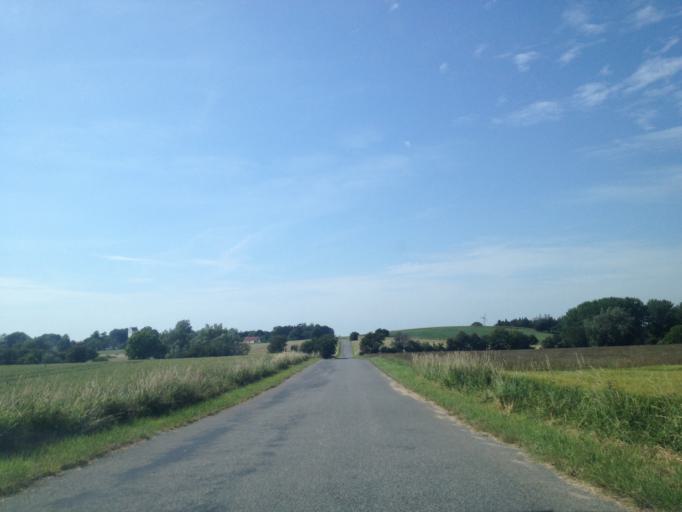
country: DK
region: Central Jutland
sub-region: Samso Kommune
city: Tranebjerg
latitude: 55.7964
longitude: 10.5689
